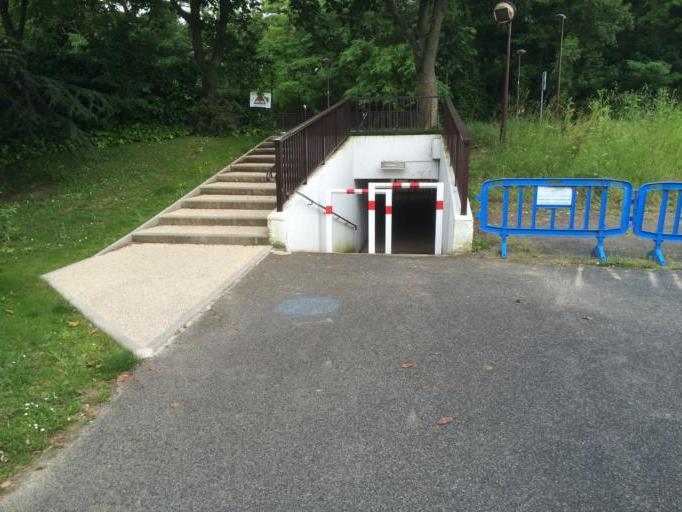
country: FR
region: Ile-de-France
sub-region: Departement de l'Essonne
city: Savigny-sur-Orge
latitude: 48.6739
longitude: 2.3638
